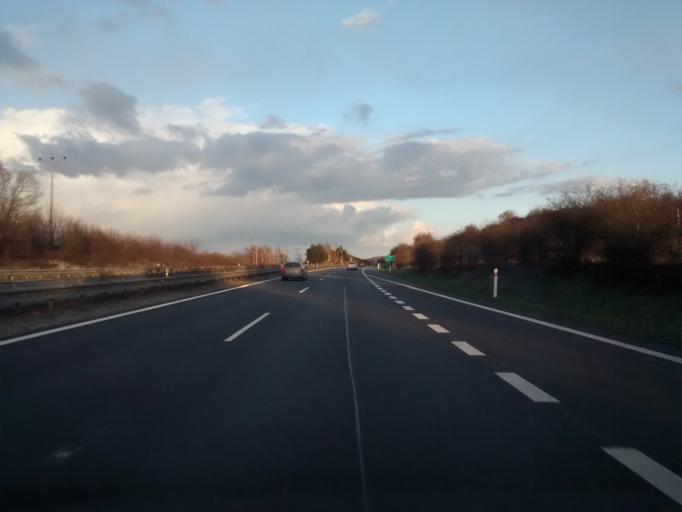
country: CZ
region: Central Bohemia
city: Prerov nad Labem
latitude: 50.1362
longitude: 14.8505
